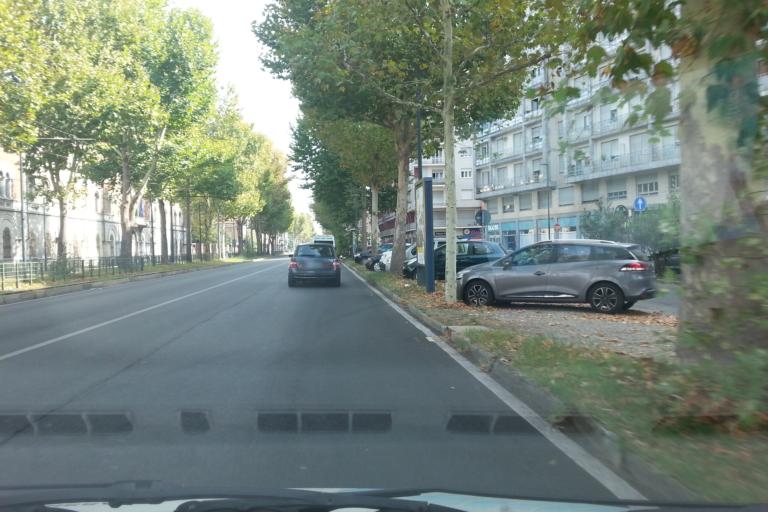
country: IT
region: Piedmont
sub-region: Provincia di Torino
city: Turin
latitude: 45.0452
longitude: 7.6604
